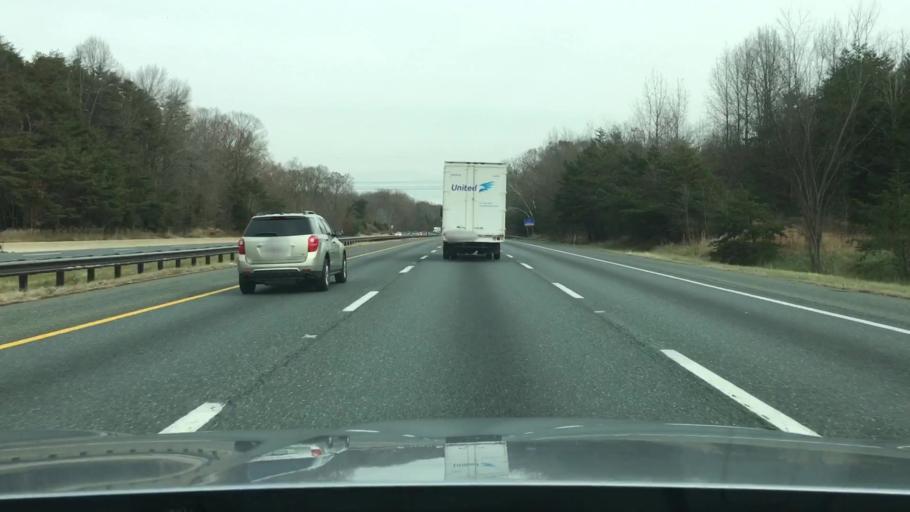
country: US
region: Maryland
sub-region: Anne Arundel County
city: Riva
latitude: 38.9716
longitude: -76.6222
